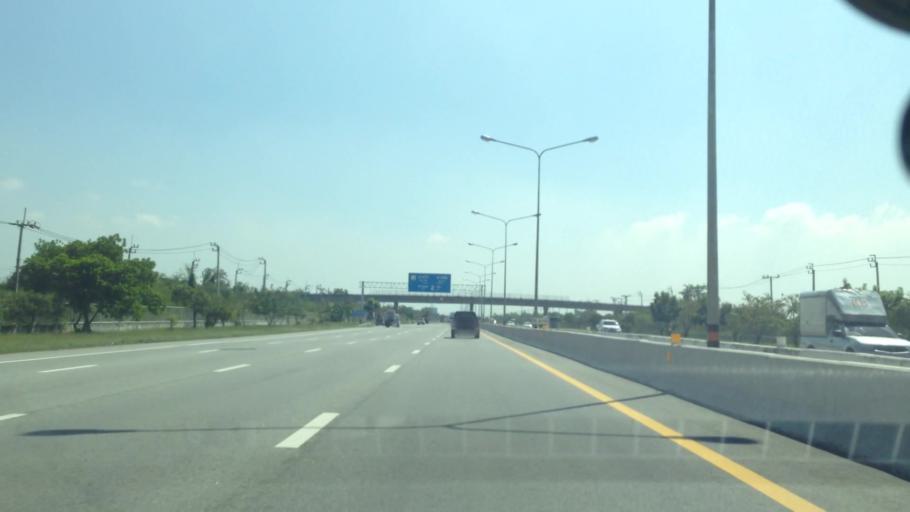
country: TH
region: Samut Prakan
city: Ban Khlong Bang Sao Thong
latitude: 13.6179
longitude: 100.9254
